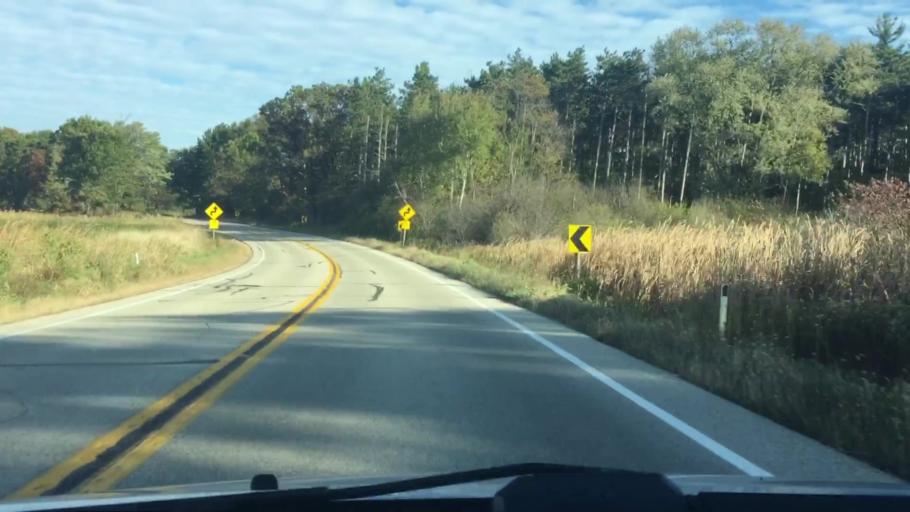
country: US
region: Wisconsin
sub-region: Waukesha County
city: Eagle
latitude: 42.9282
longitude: -88.4660
